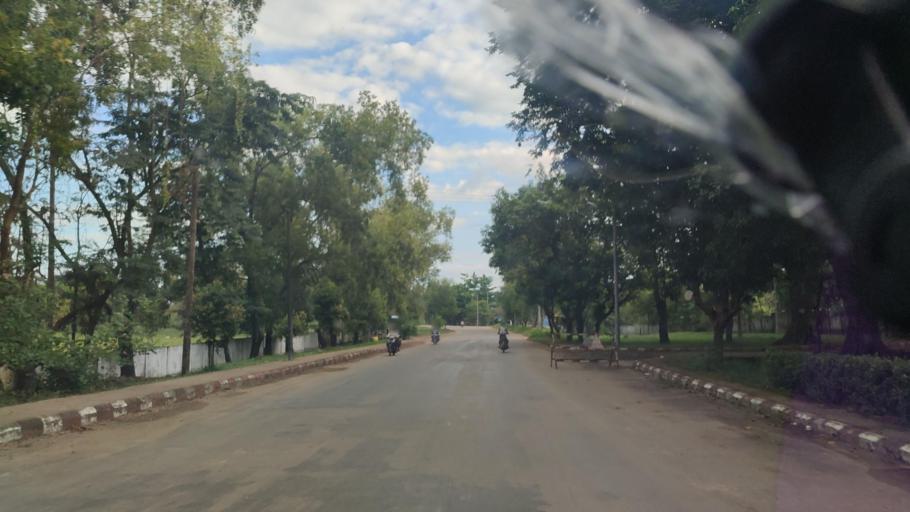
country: MM
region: Magway
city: Minbu
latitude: 19.7563
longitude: 94.0332
